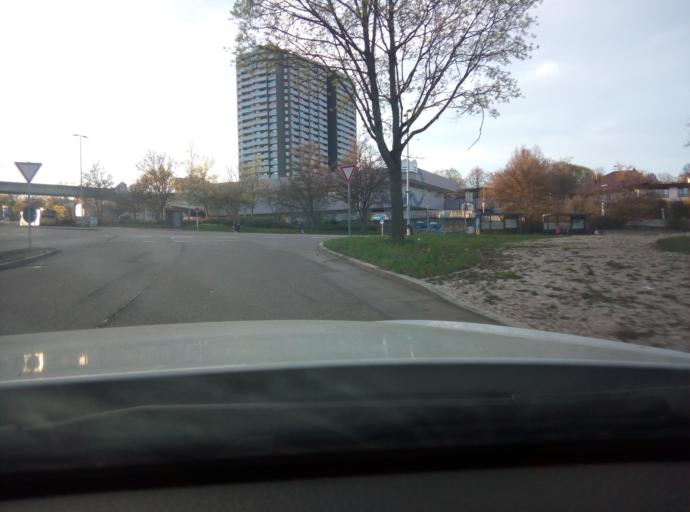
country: DE
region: Baden-Wuerttemberg
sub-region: Tuebingen Region
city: Tuebingen
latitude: 48.5416
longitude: 9.0616
